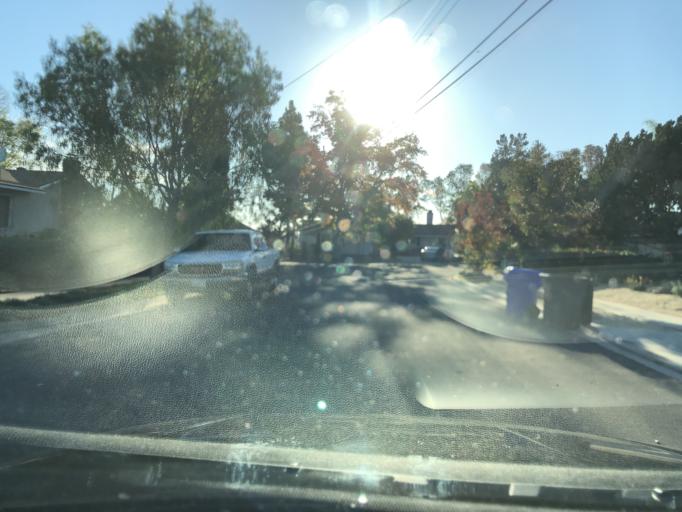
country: US
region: California
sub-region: San Diego County
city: La Jolla
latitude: 32.8194
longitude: -117.1907
